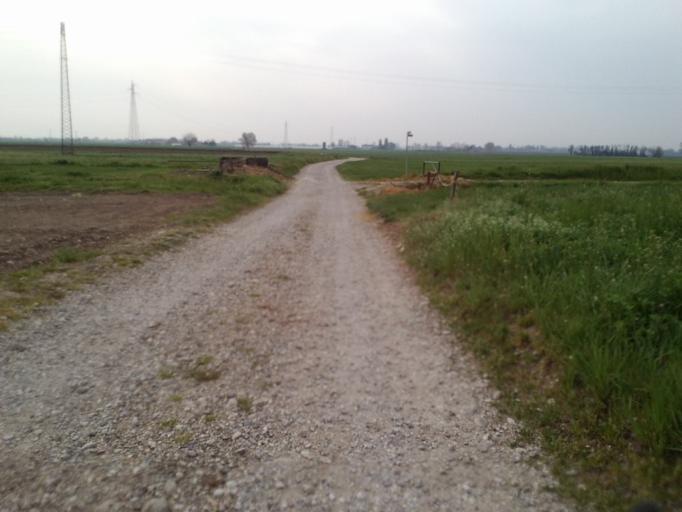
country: IT
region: Veneto
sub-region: Provincia di Verona
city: Villafranca di Verona
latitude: 45.3364
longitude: 10.8589
